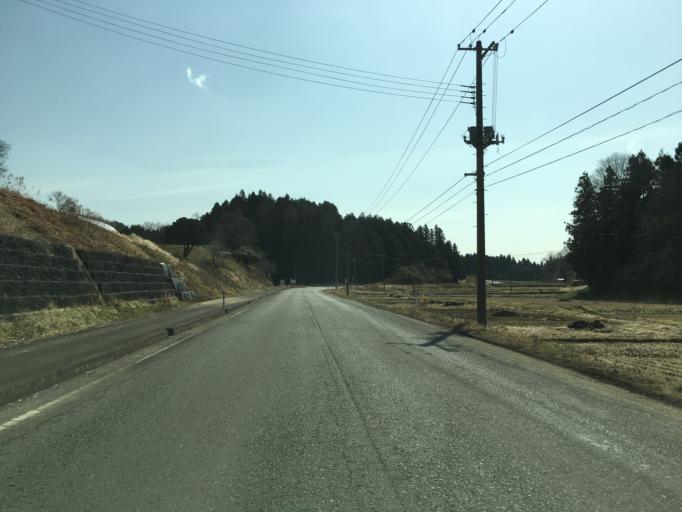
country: JP
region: Fukushima
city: Ishikawa
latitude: 37.1341
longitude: 140.4094
